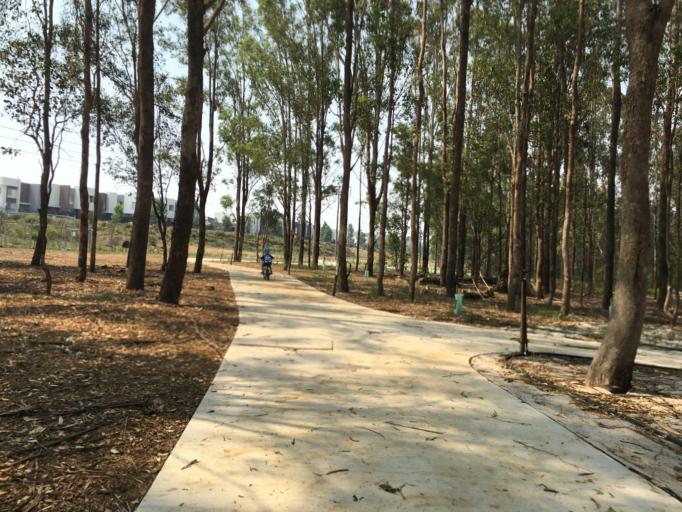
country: AU
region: New South Wales
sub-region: Campbelltown Municipality
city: Denham Court
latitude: -33.9772
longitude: 150.8141
